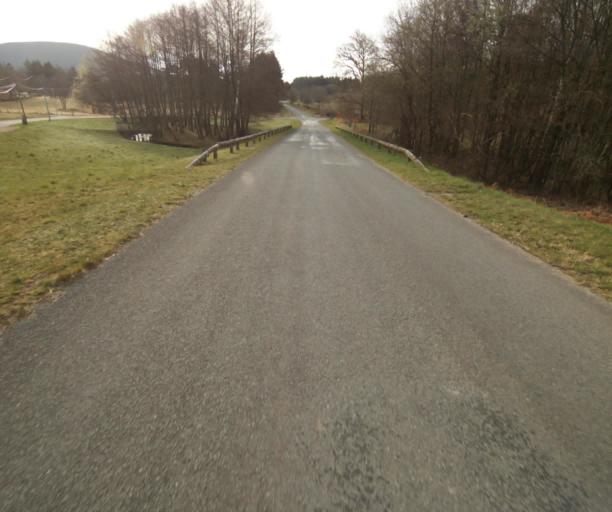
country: FR
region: Limousin
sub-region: Departement de la Correze
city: Treignac
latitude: 45.4729
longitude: 1.7967
